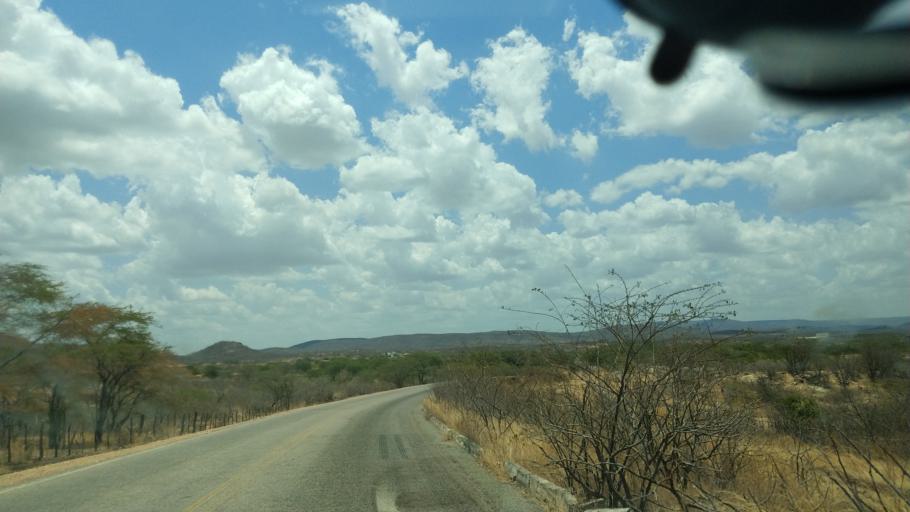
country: BR
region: Rio Grande do Norte
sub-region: Currais Novos
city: Currais Novos
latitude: -6.2777
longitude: -36.5381
